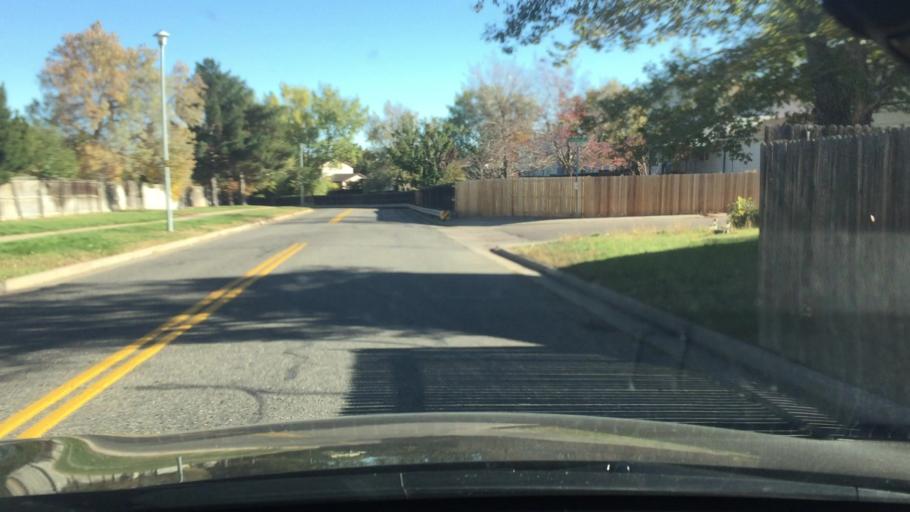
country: US
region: Colorado
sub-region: Arapahoe County
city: Dove Valley
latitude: 39.6289
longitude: -104.7951
